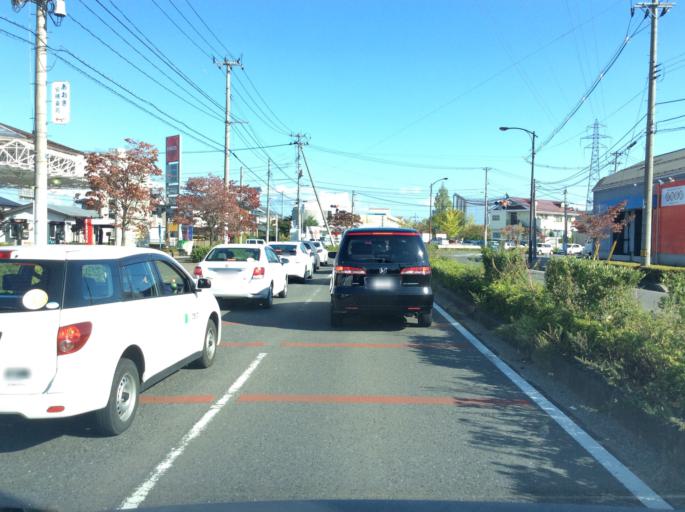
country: JP
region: Fukushima
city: Koriyama
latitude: 37.3676
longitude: 140.3618
